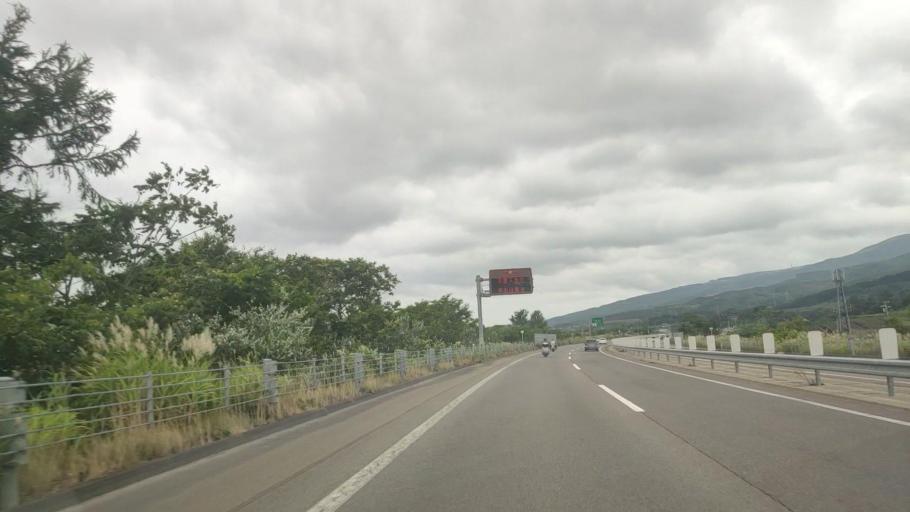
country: JP
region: Hokkaido
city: Nanae
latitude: 41.8626
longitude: 140.7317
